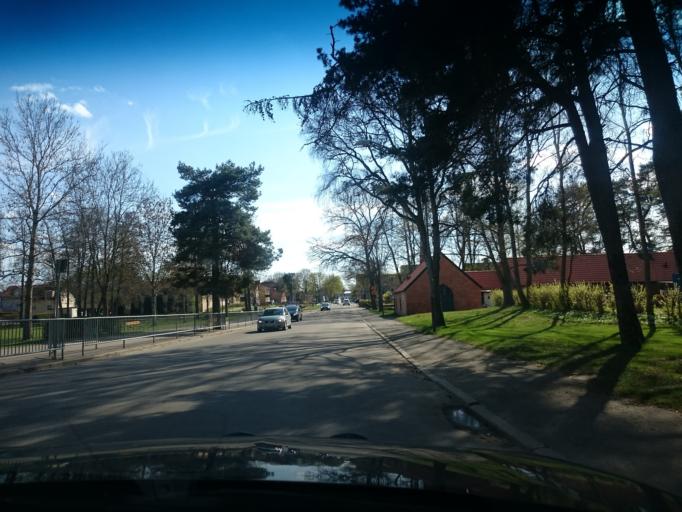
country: SE
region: Joenkoeping
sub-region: Vetlanda Kommun
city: Vetlanda
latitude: 57.4309
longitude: 15.0845
